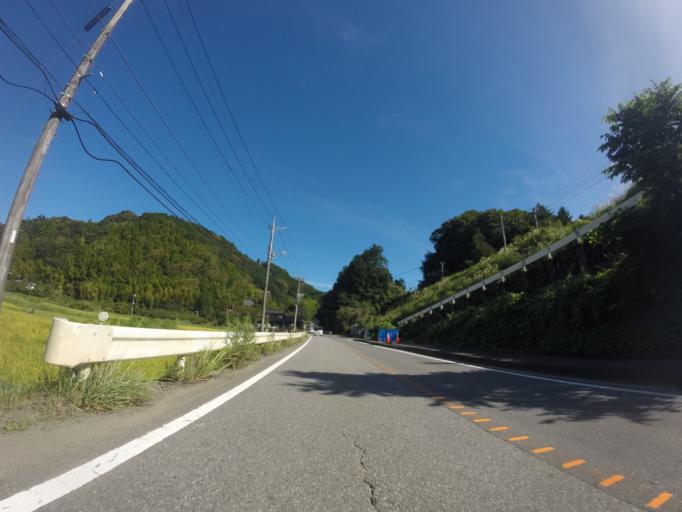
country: JP
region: Shizuoka
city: Fujinomiya
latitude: 35.3417
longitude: 138.4500
